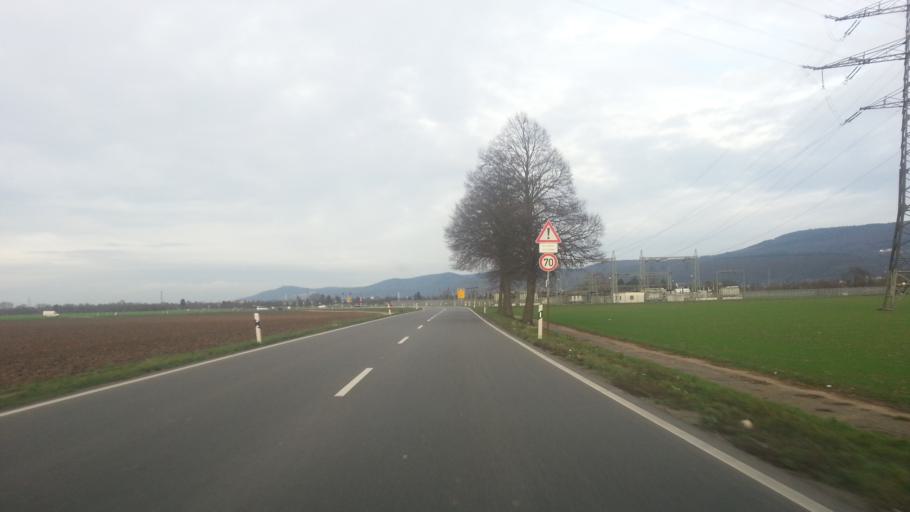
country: DE
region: Baden-Wuerttemberg
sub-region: Karlsruhe Region
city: Sandhausen
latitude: 49.3575
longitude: 8.6616
